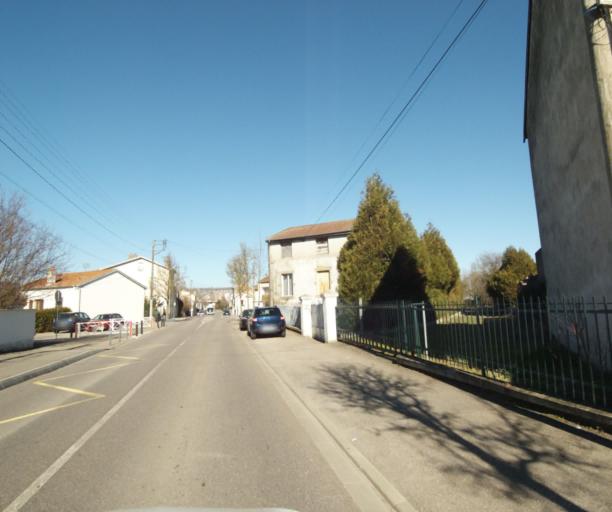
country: FR
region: Lorraine
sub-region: Departement de Meurthe-et-Moselle
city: Tomblaine
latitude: 48.6910
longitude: 6.2109
